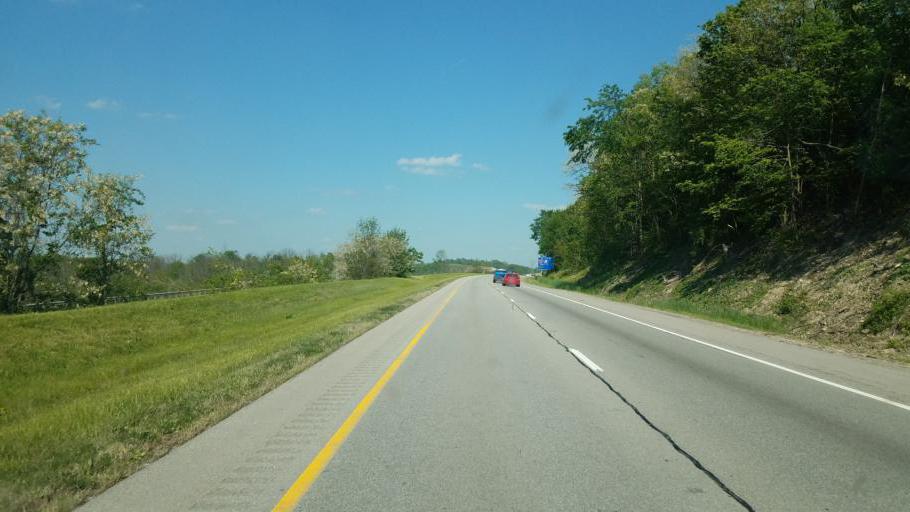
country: US
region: Ohio
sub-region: Muskingum County
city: New Concord
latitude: 39.9802
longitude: -81.7449
